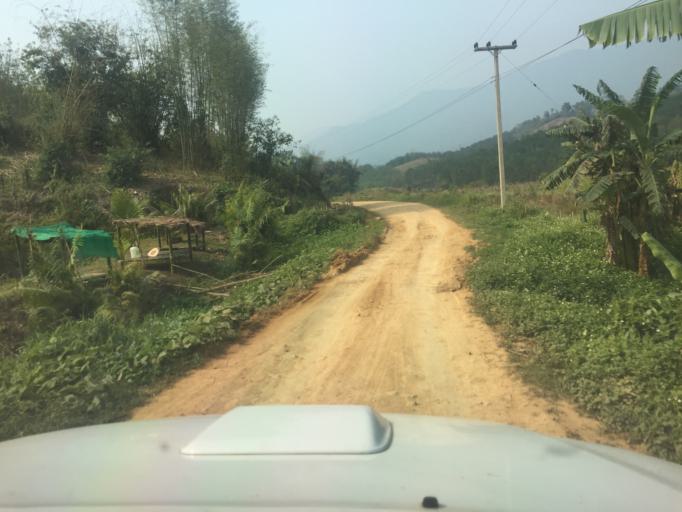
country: TH
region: Phayao
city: Phu Sang
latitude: 19.6546
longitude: 100.5277
